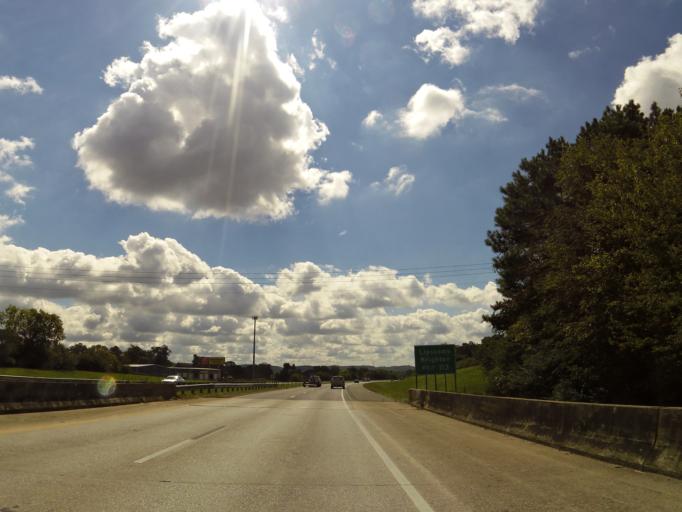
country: US
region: Alabama
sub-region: Jefferson County
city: Brighton
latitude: 33.4367
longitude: -86.9551
